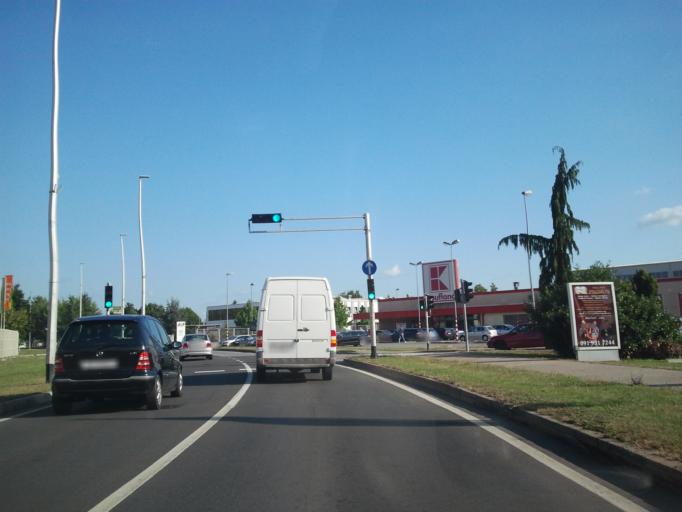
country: HR
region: Zagrebacka
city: Gradici
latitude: 45.7193
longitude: 16.0545
